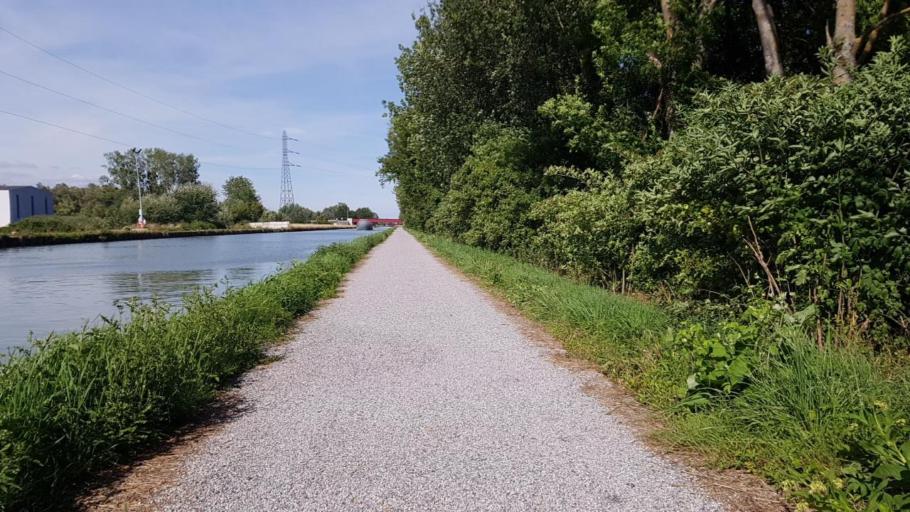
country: FR
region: Picardie
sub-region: Departement de l'Aisne
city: Tergnier
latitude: 49.6350
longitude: 3.2759
